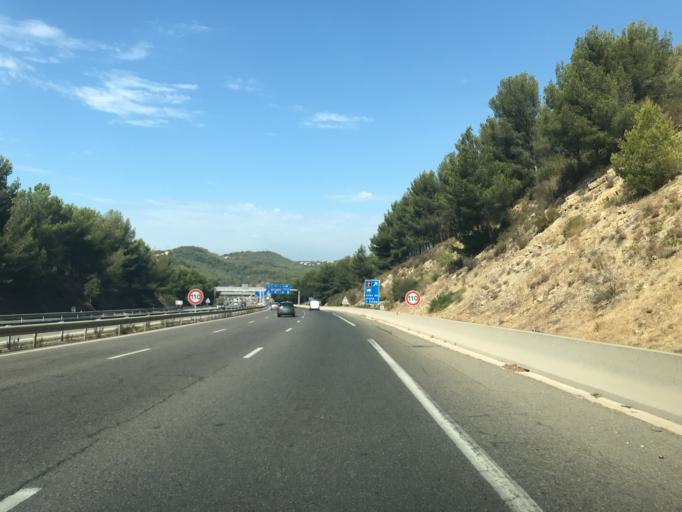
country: FR
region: Provence-Alpes-Cote d'Azur
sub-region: Departement du Var
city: Sanary-sur-Mer
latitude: 43.1463
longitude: 5.7811
